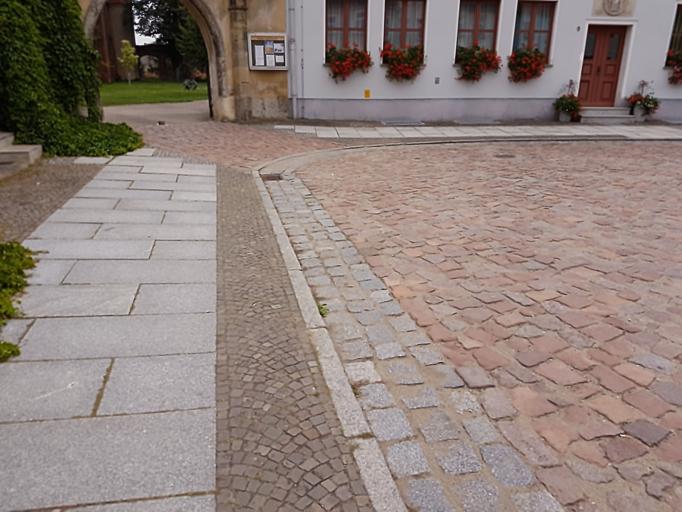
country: DE
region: Brandenburg
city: Muhlberg
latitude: 51.4357
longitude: 13.2185
